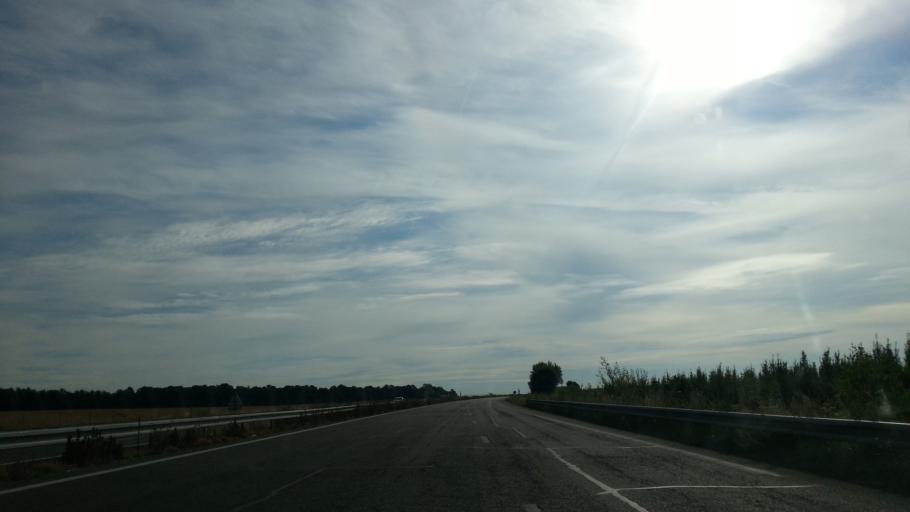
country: FR
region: Picardie
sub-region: Departement de l'Aisne
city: Montreuil-aux-Lions
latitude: 49.0391
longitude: 3.1967
